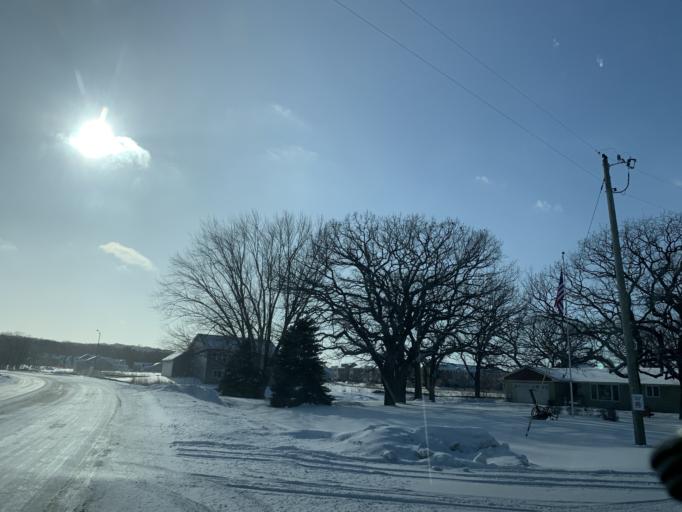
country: US
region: Minnesota
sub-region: Scott County
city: Prior Lake
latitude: 44.7756
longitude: -93.4073
